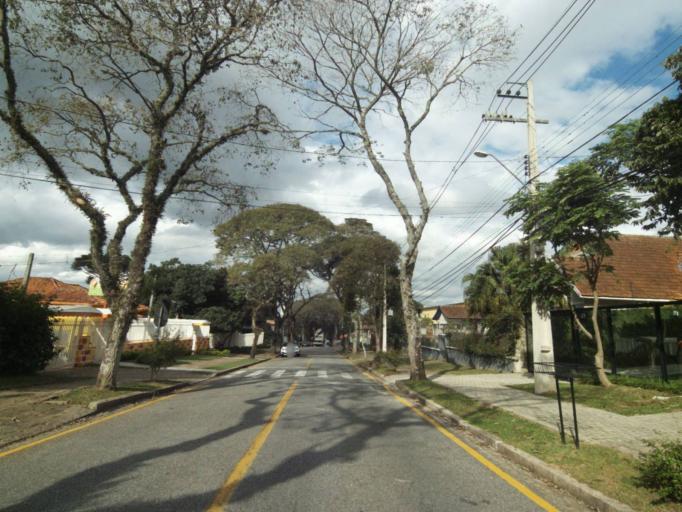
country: BR
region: Parana
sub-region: Curitiba
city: Curitiba
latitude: -25.4219
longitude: -49.2800
